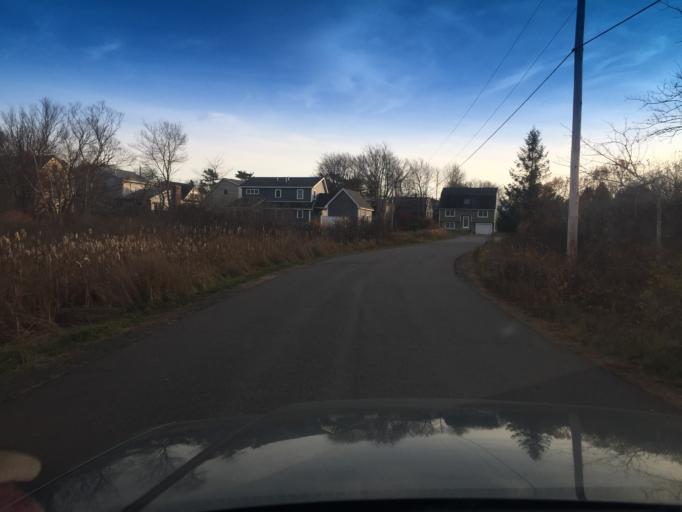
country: US
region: Maine
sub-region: York County
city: York Beach
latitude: 43.1718
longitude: -70.6049
